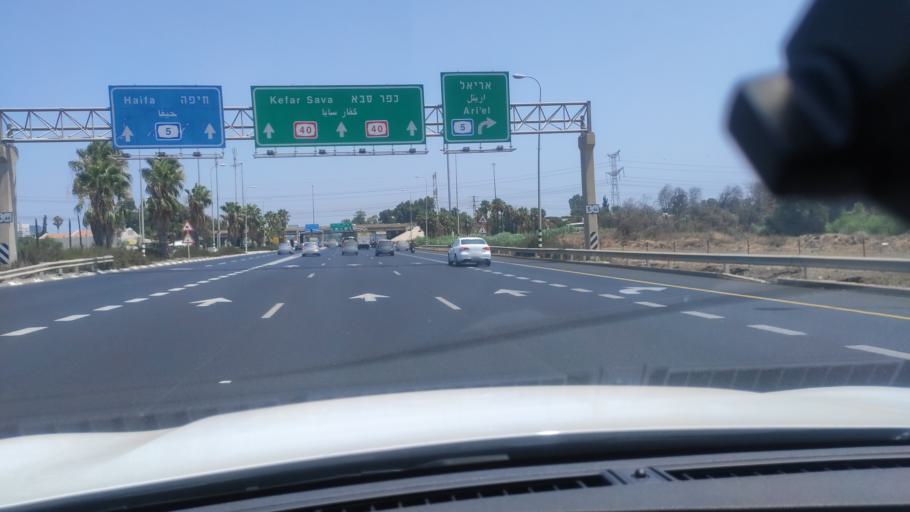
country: IL
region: Central District
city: Petah Tiqwa
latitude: 32.1191
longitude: 34.9033
